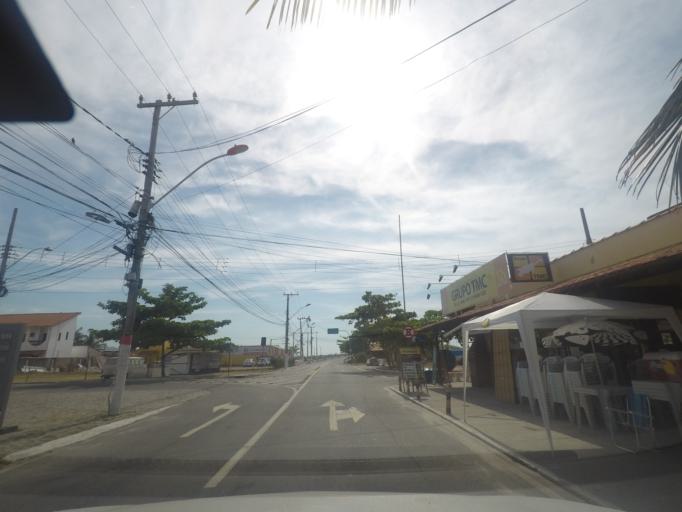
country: BR
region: Rio de Janeiro
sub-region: Marica
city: Marica
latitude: -22.9594
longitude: -42.8150
